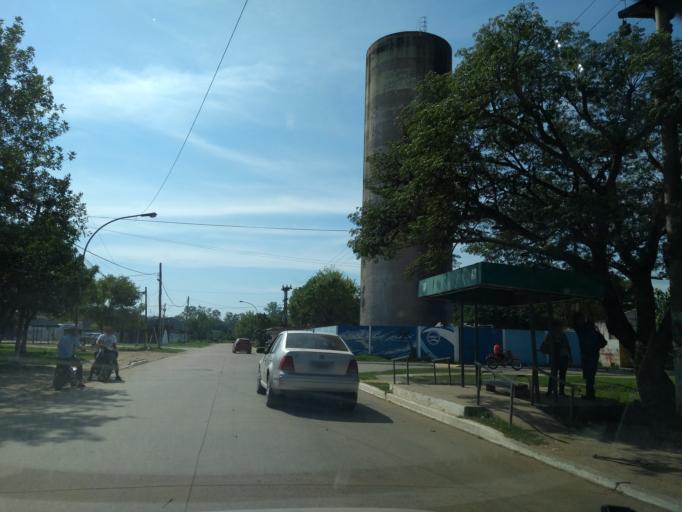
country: AR
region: Chaco
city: Barranqueras
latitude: -27.4644
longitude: -58.9493
